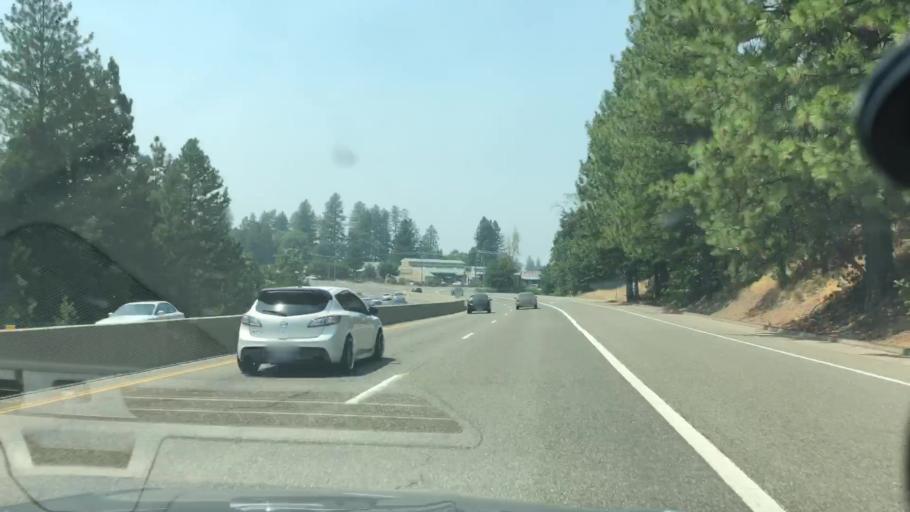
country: US
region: California
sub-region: El Dorado County
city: Camino
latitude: 38.7396
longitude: -120.6944
